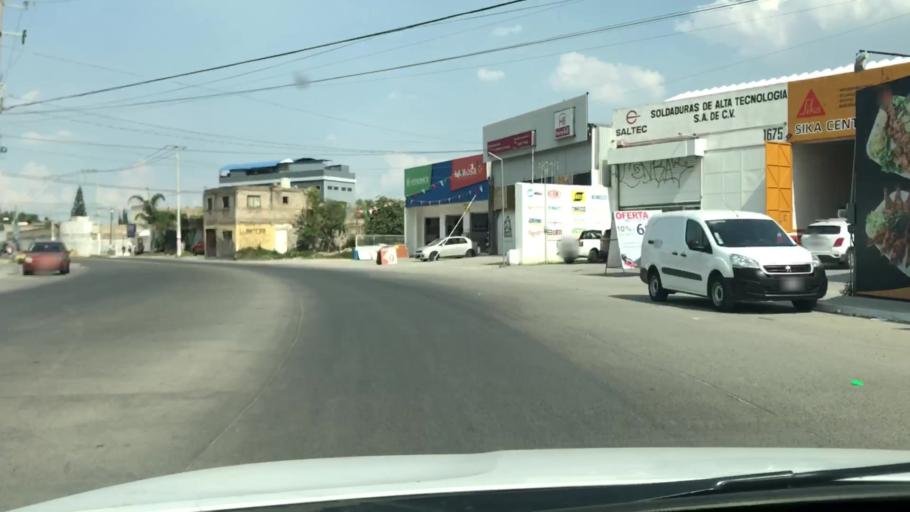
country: MX
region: Jalisco
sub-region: Tlajomulco de Zuniga
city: Palomar
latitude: 20.6488
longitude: -103.4573
